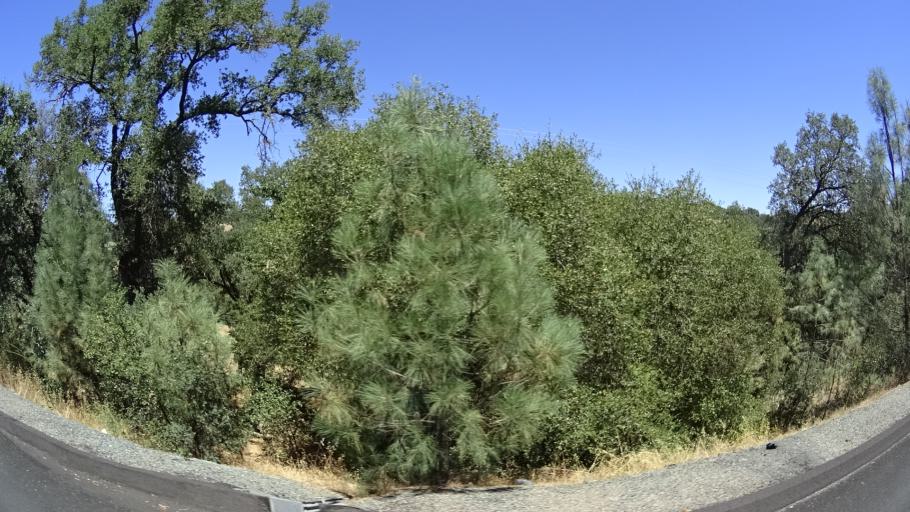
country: US
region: California
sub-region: Calaveras County
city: San Andreas
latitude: 38.2246
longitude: -120.7016
